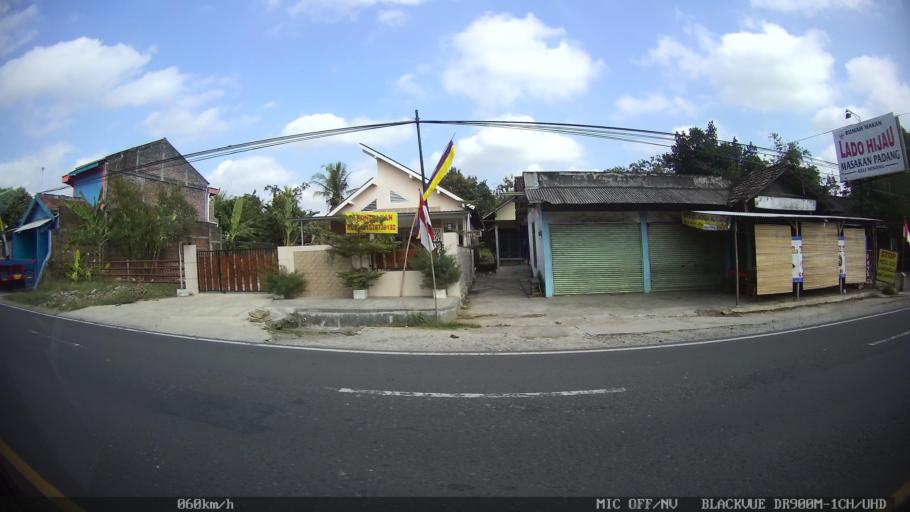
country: ID
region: Daerah Istimewa Yogyakarta
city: Srandakan
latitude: -7.8415
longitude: 110.2187
